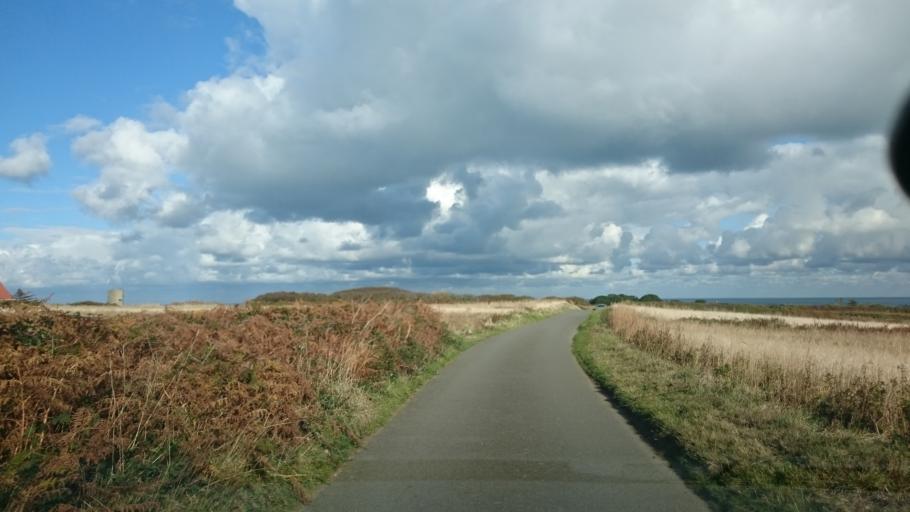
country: GG
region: St Peter Port
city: Saint Peter Port
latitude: 49.4292
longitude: -2.6682
